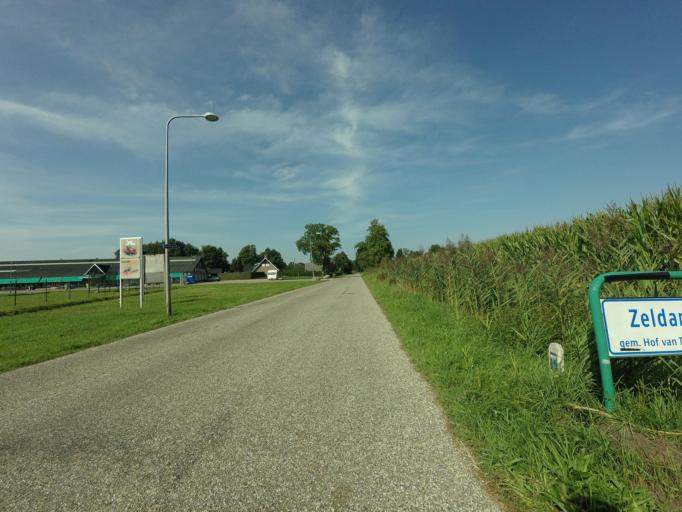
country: NL
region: Overijssel
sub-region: Gemeente Hof van Twente
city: Hengevelde
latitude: 52.2458
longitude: 6.6350
